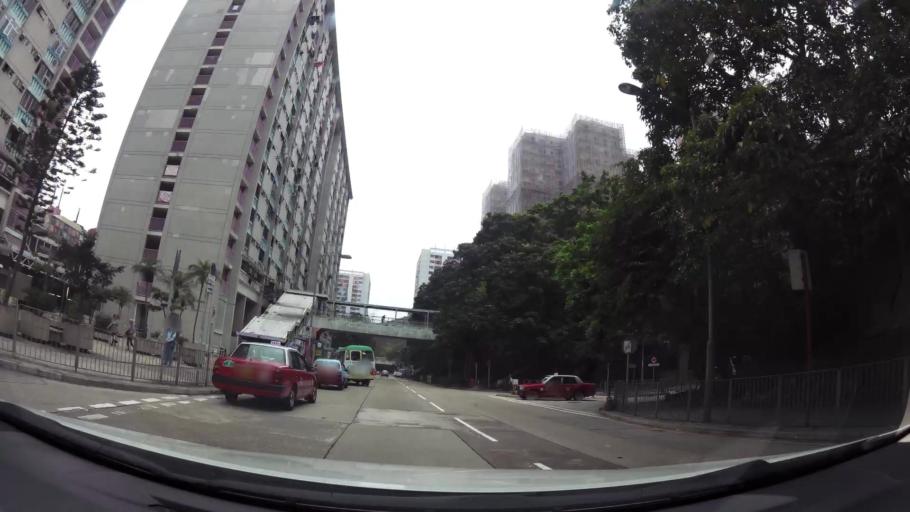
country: HK
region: Kowloon City
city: Kowloon
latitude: 22.3315
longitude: 114.2264
